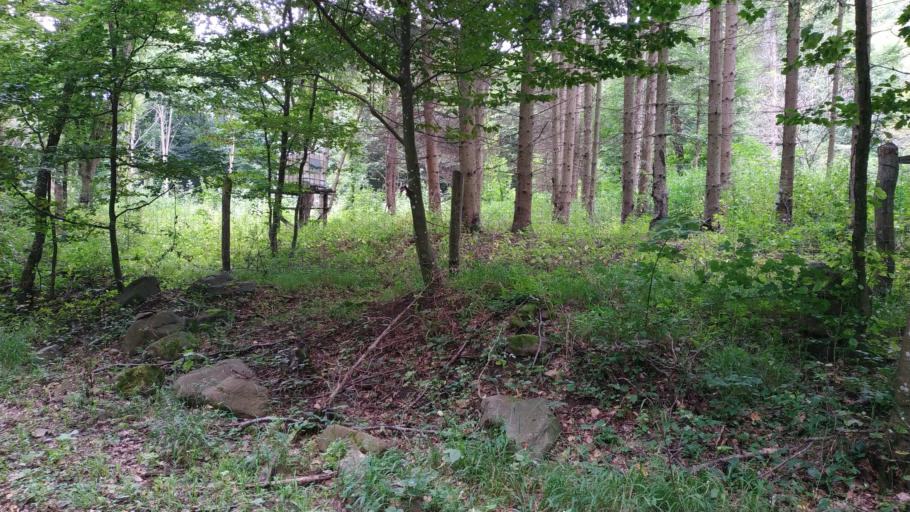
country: HU
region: Heves
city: Paradsasvar
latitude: 47.8858
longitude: 19.9139
